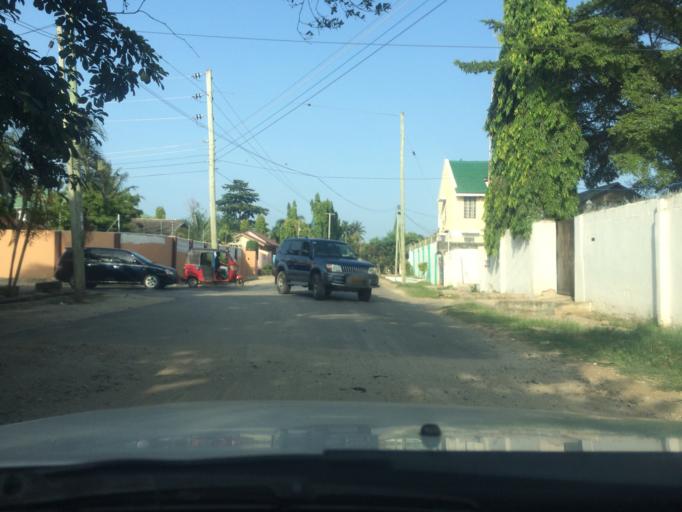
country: TZ
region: Dar es Salaam
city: Magomeni
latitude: -6.7734
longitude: 39.2570
